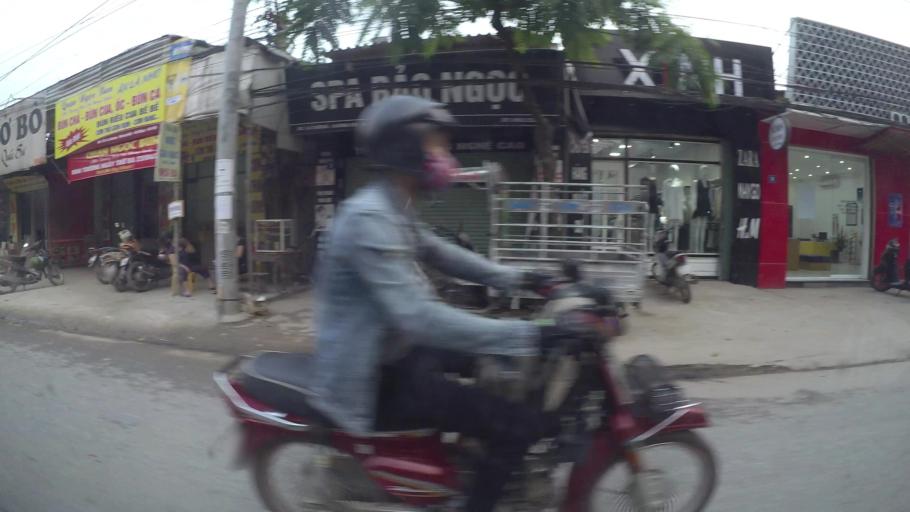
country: VN
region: Ha Noi
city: Ha Dong
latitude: 20.9918
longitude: 105.7303
